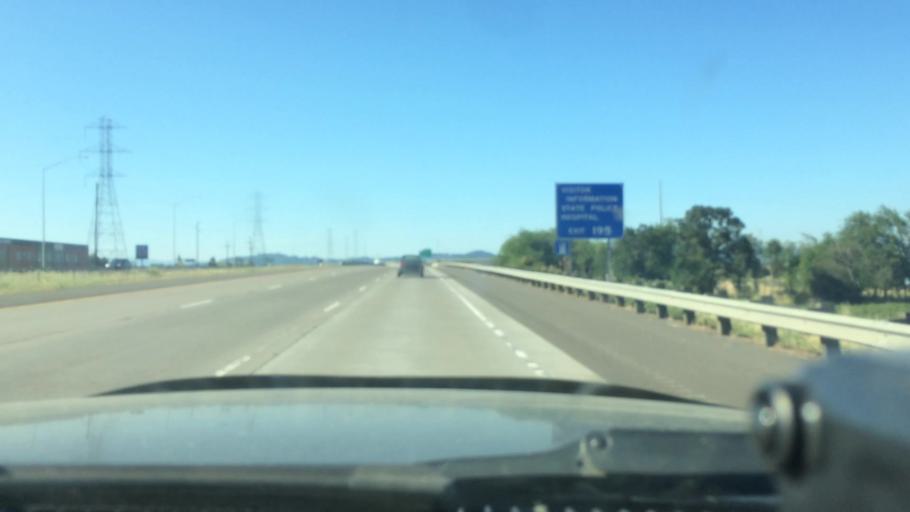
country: US
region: Oregon
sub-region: Lane County
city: Coburg
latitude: 44.0918
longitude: -123.0460
